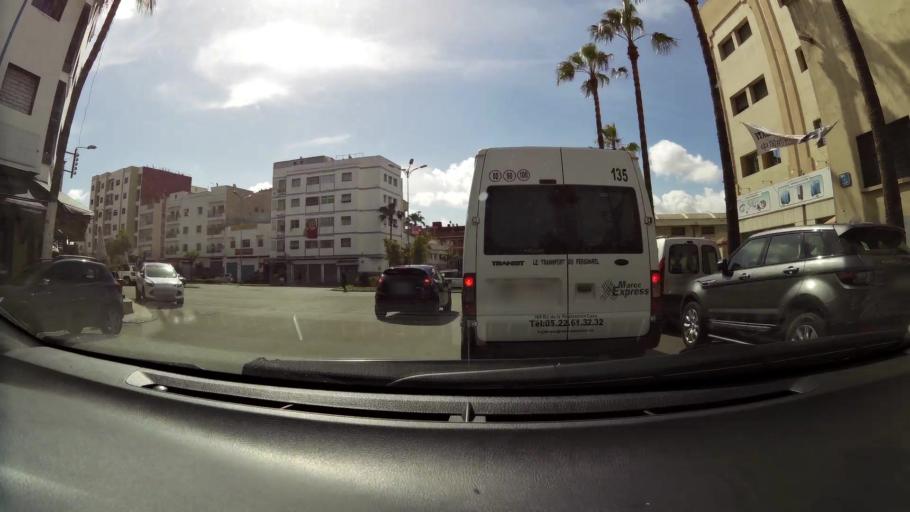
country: MA
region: Grand Casablanca
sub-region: Casablanca
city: Casablanca
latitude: 33.5880
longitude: -7.5766
